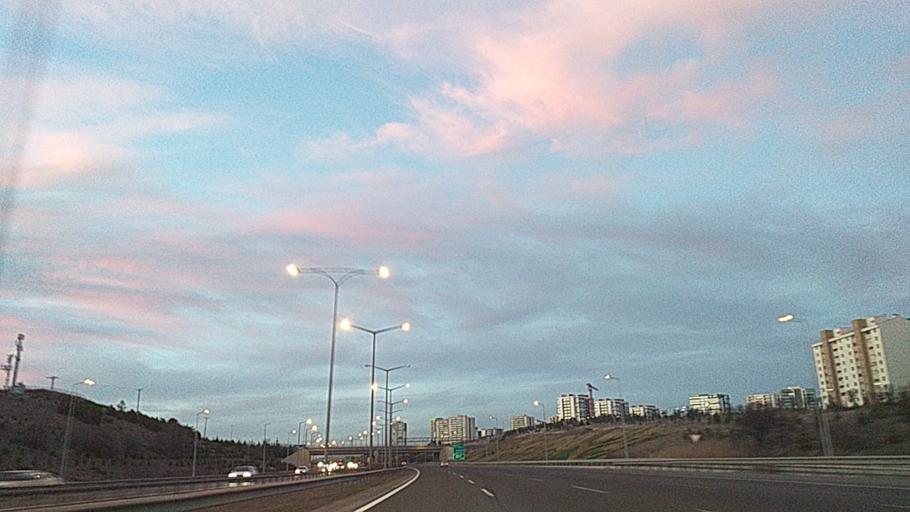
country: TR
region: Ankara
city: Etimesgut
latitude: 39.9936
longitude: 32.6372
